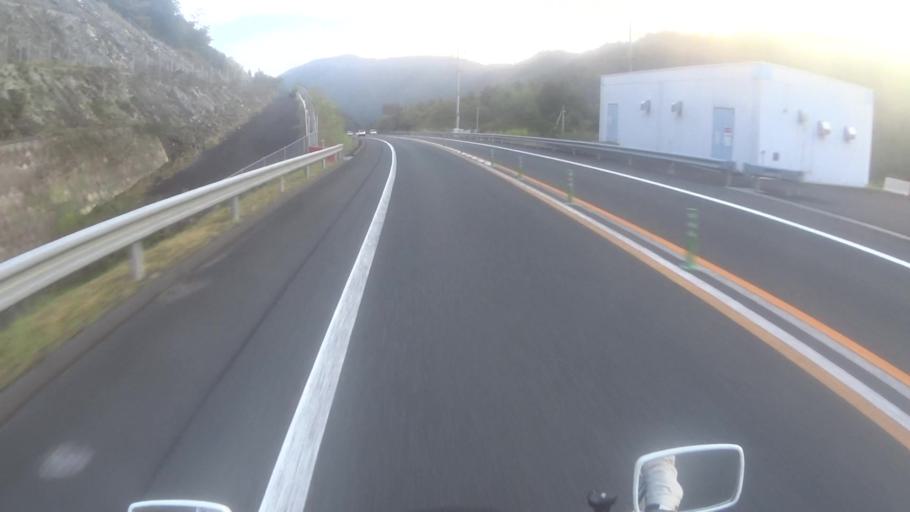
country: JP
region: Kyoto
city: Miyazu
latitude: 35.4661
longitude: 135.1735
